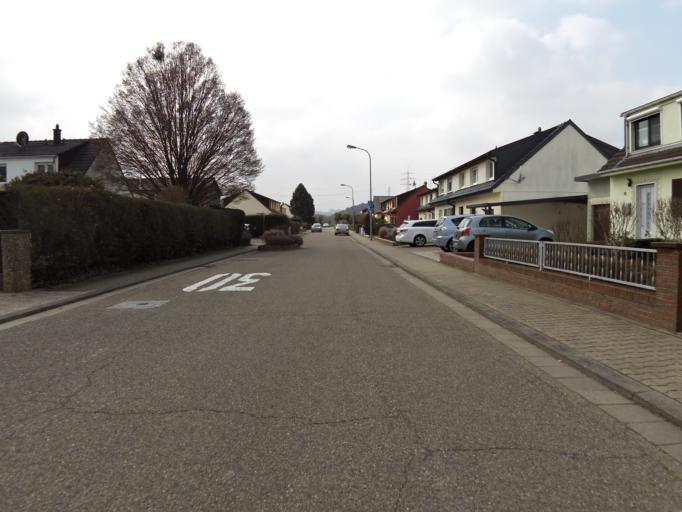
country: DE
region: Rheinland-Pfalz
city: Grunstadt
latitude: 49.5796
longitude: 8.1583
